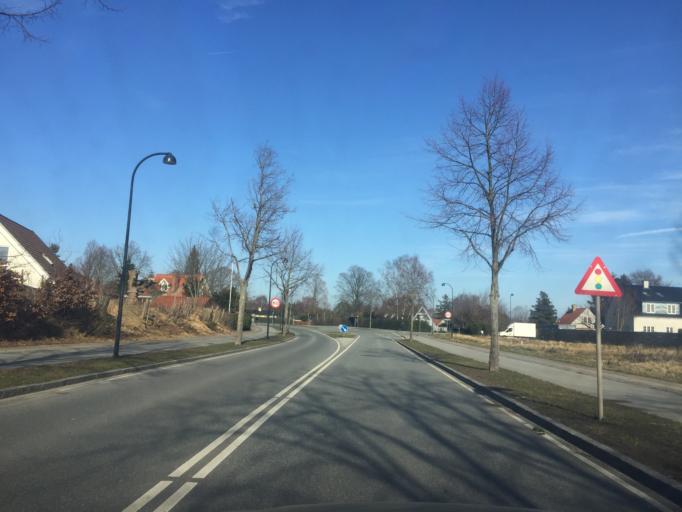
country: DK
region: Capital Region
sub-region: Rudersdal Kommune
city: Trorod
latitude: 55.8446
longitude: 12.5324
